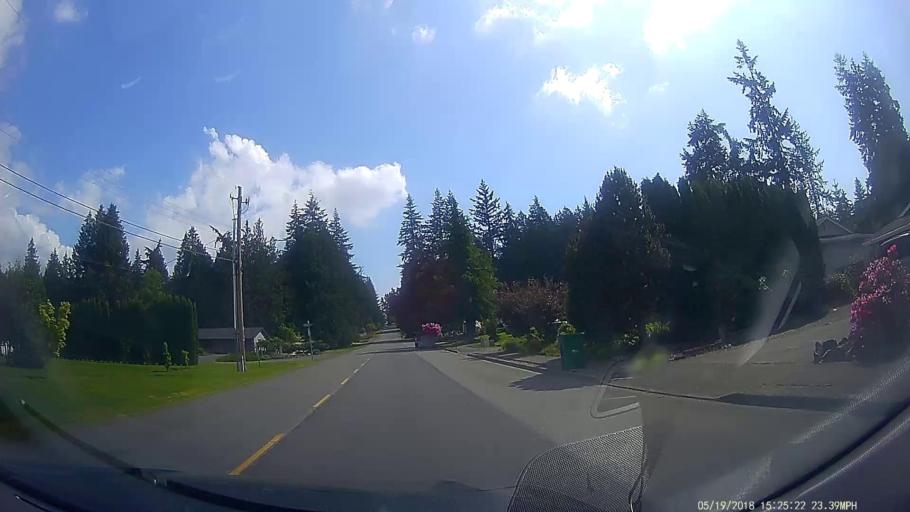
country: US
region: Washington
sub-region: Skagit County
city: Mount Vernon
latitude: 48.4307
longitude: -122.3074
